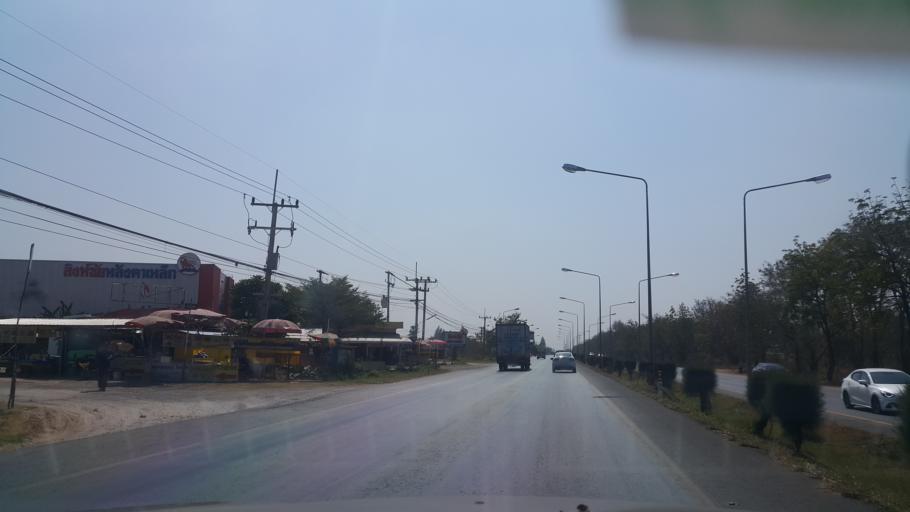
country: TH
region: Khon Kaen
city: Ban Phai
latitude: 16.0174
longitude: 102.7071
